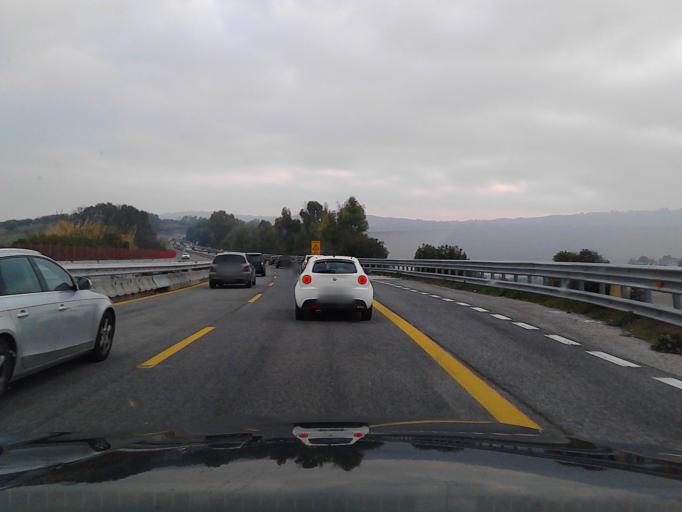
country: IT
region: Abruzzo
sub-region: Provincia di Teramo
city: Tortoreto Lido
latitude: 42.7907
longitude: 13.9339
